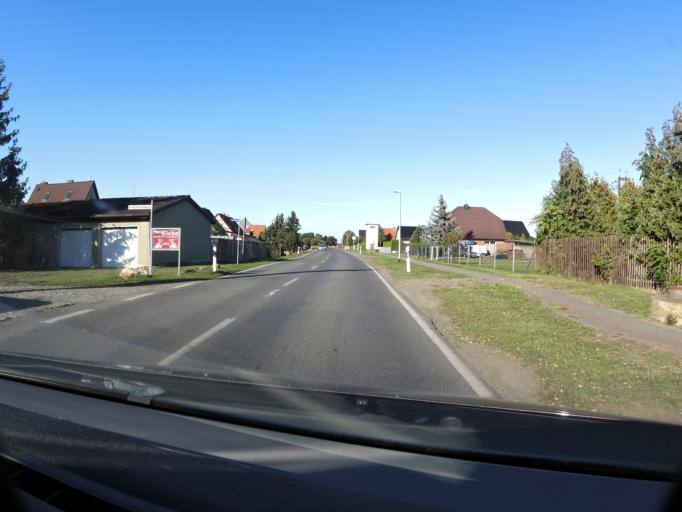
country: DE
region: Saxony-Anhalt
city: Wegeleben
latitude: 51.8935
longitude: 11.1865
